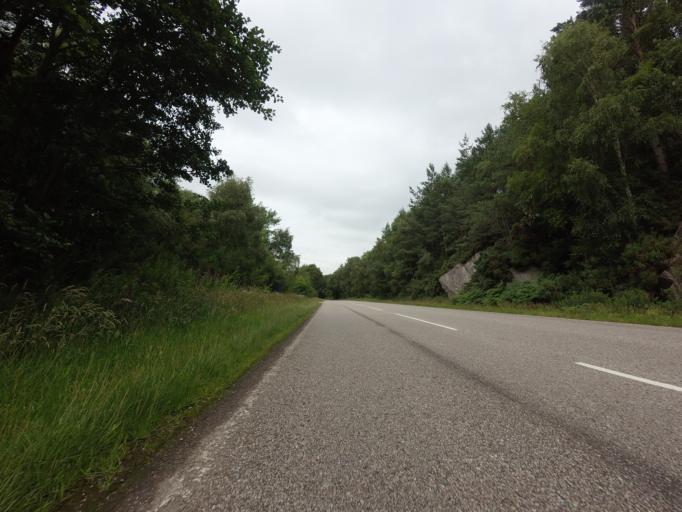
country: GB
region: Scotland
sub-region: Highland
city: Alness
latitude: 57.9079
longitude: -4.3627
